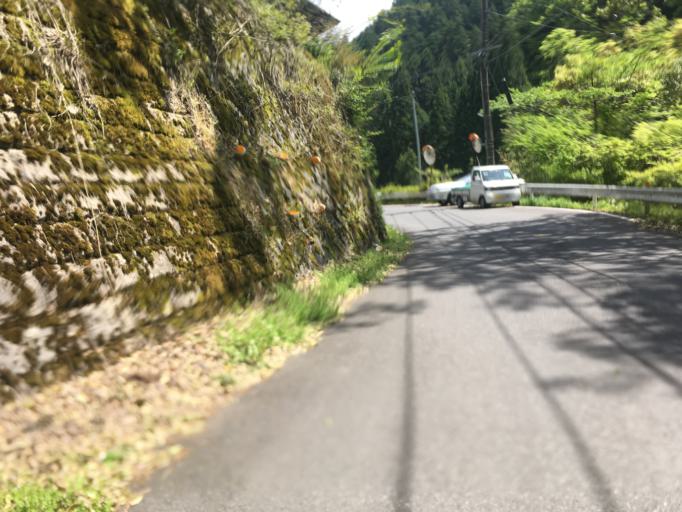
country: JP
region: Kyoto
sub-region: Kyoto-shi
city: Kamigyo-ku
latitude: 35.1080
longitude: 135.7249
